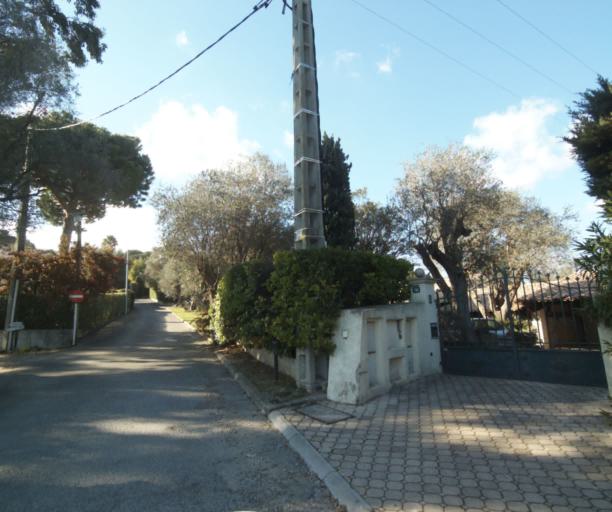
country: FR
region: Provence-Alpes-Cote d'Azur
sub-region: Departement des Alpes-Maritimes
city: Biot
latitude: 43.6128
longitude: 7.1013
